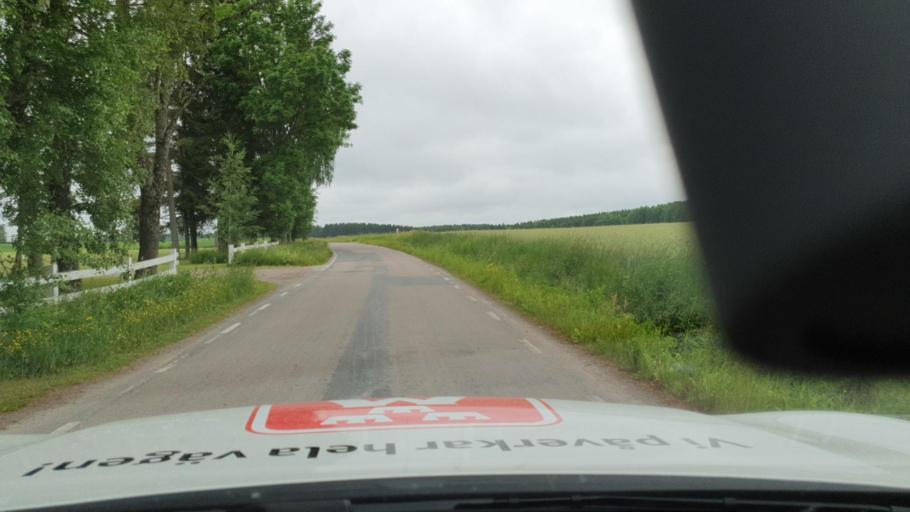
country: SE
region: Vaestra Goetaland
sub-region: Tibro Kommun
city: Tibro
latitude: 58.4031
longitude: 14.1314
